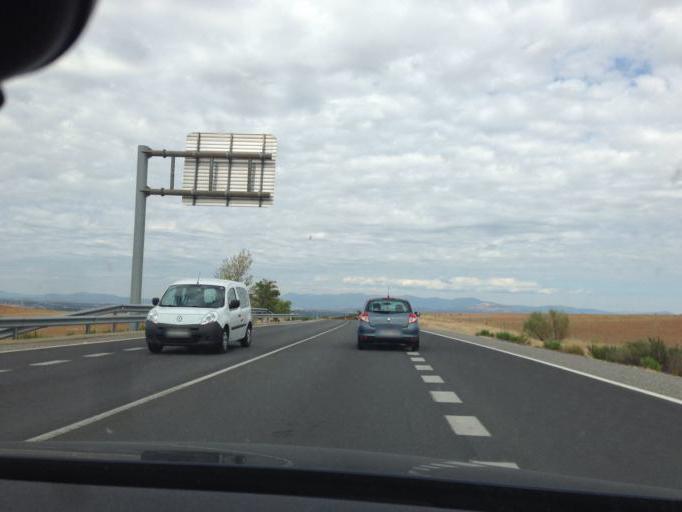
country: ES
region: Madrid
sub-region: Provincia de Madrid
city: Cobena
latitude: 40.5705
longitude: -3.5221
